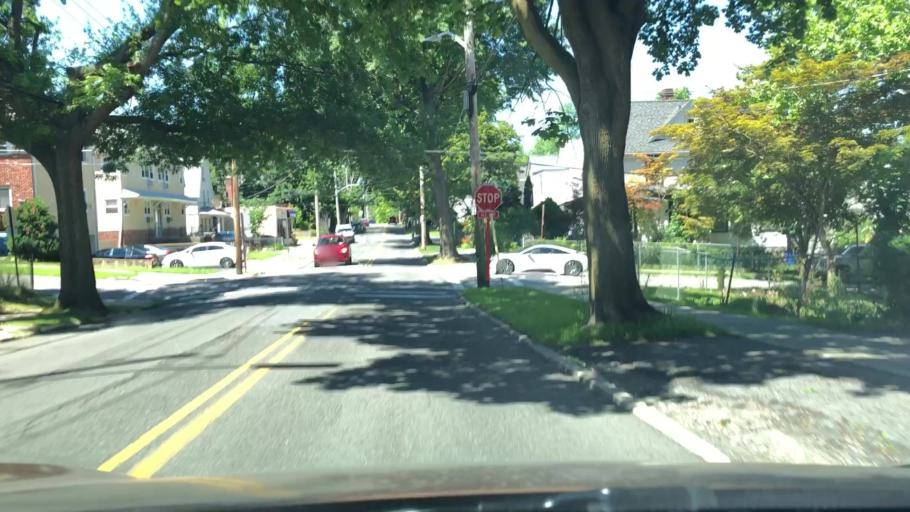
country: US
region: New York
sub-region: Westchester County
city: Hartsdale
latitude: 41.0299
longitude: -73.7852
